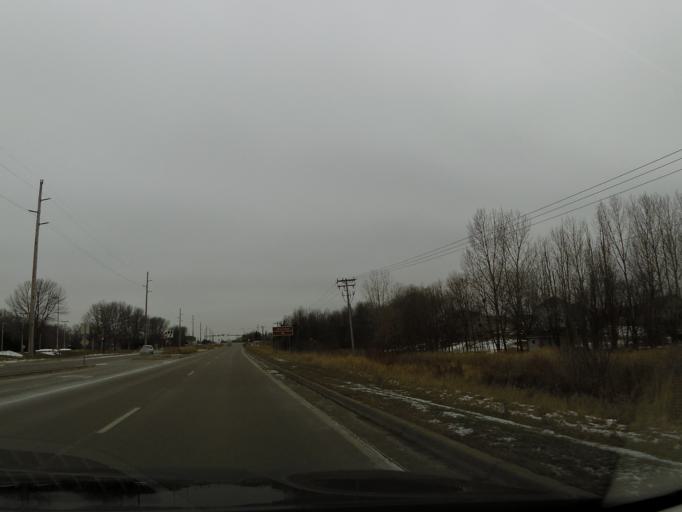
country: US
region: Minnesota
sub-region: Carver County
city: Waconia
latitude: 44.8369
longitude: -93.8040
